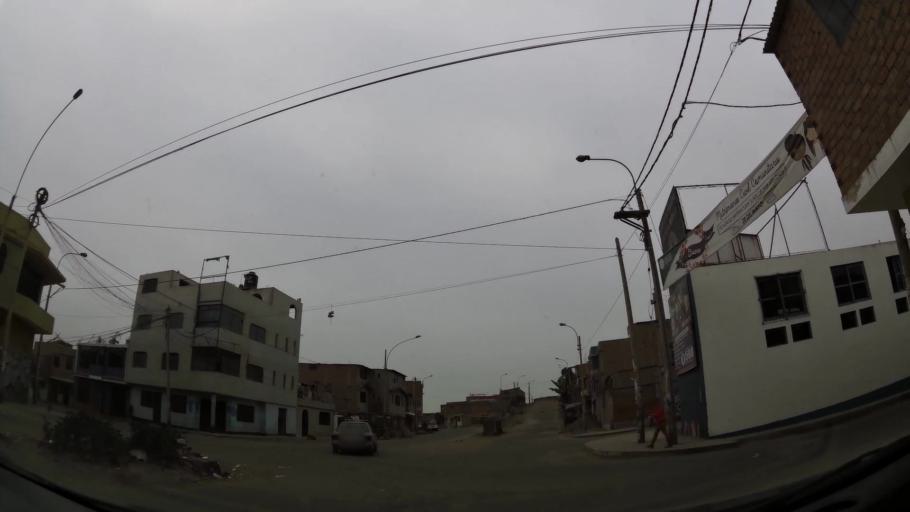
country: PE
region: Lima
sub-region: Lima
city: Surco
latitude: -12.1890
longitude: -76.9794
